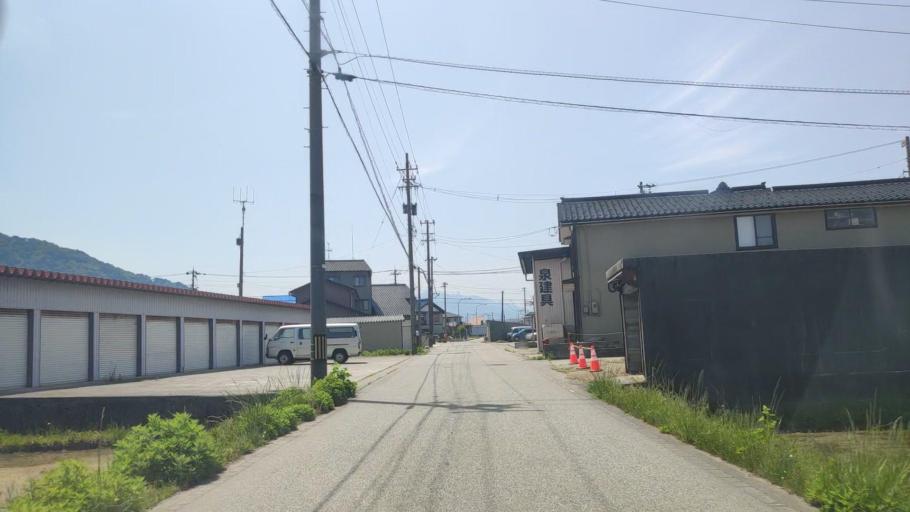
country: JP
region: Toyama
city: Nyuzen
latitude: 36.9584
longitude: 137.5680
